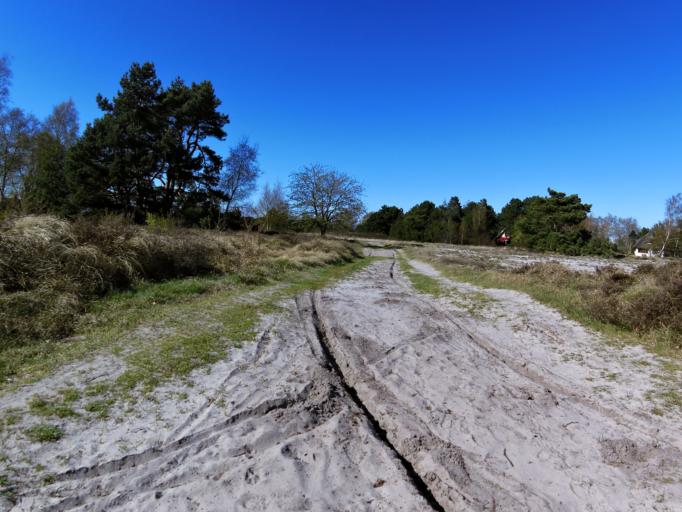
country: DE
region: Mecklenburg-Vorpommern
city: Hiddensee
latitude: 54.5456
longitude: 13.0983
